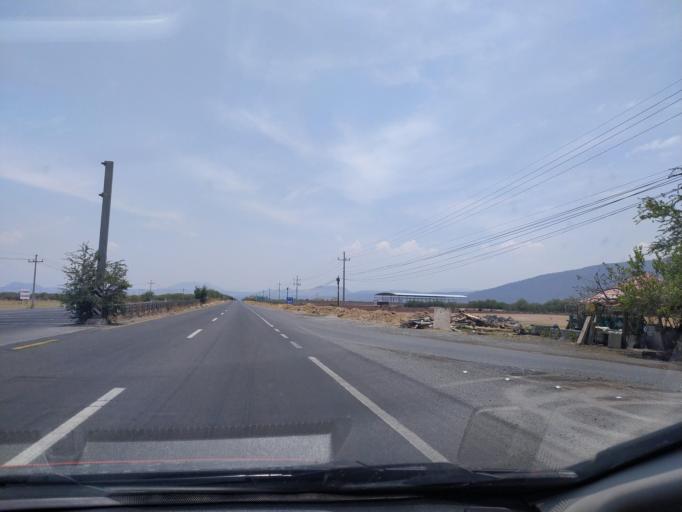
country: MX
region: Jalisco
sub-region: Acatlan de Juarez
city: Villa de los Ninos
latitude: 20.3493
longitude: -103.5914
